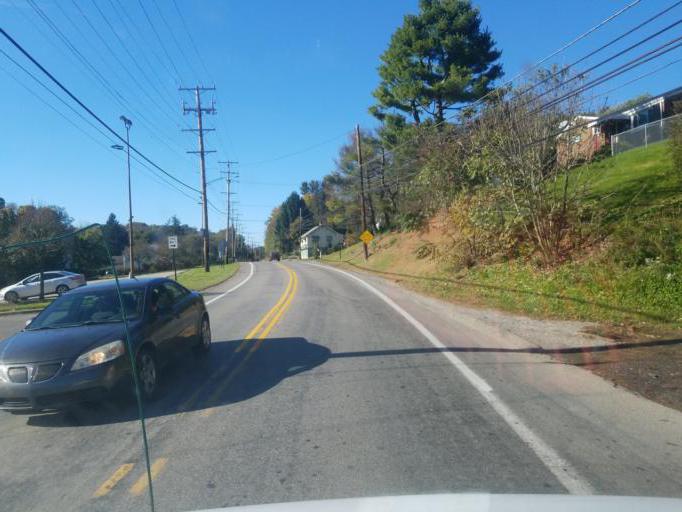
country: US
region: Pennsylvania
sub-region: Allegheny County
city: Imperial
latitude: 40.4522
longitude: -80.2519
